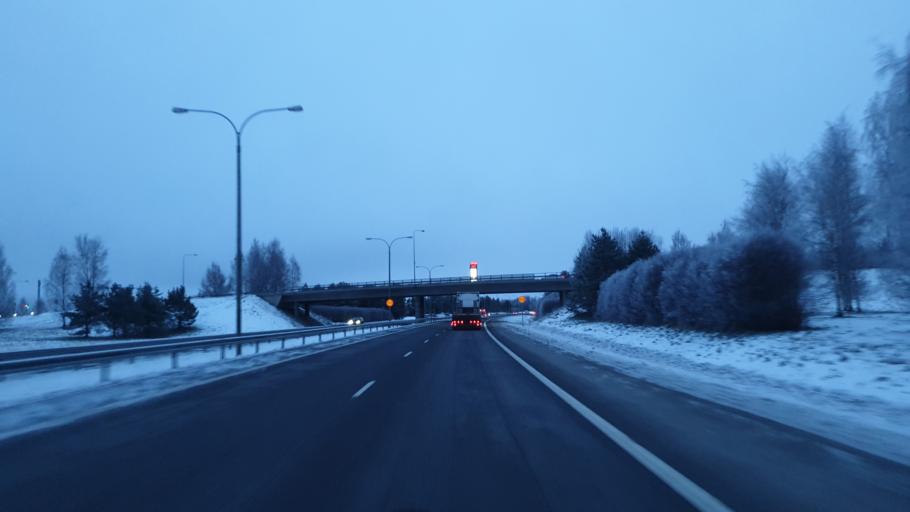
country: FI
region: Northern Ostrobothnia
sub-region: Oulu
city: Kempele
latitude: 64.9071
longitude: 25.5361
